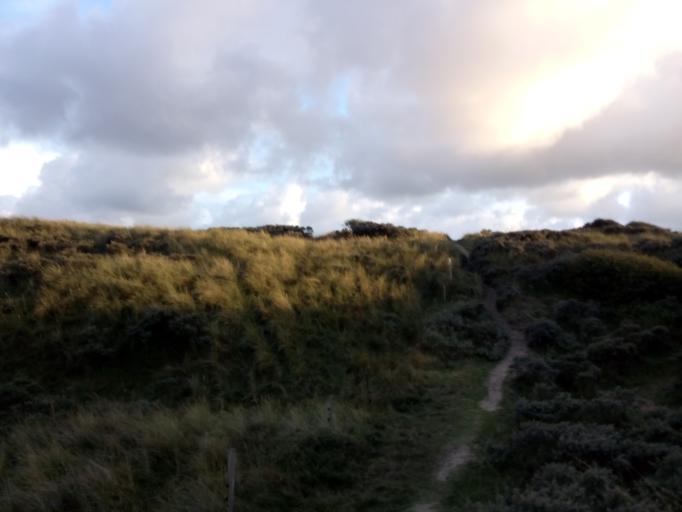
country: DK
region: North Denmark
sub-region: Hjorring Kommune
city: Vra
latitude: 57.4539
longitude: 9.7798
